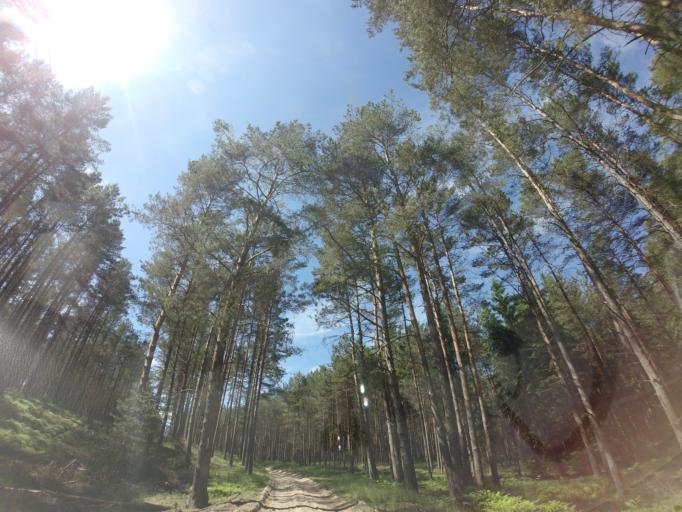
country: PL
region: West Pomeranian Voivodeship
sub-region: Powiat choszczenski
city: Drawno
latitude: 53.1278
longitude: 15.7925
